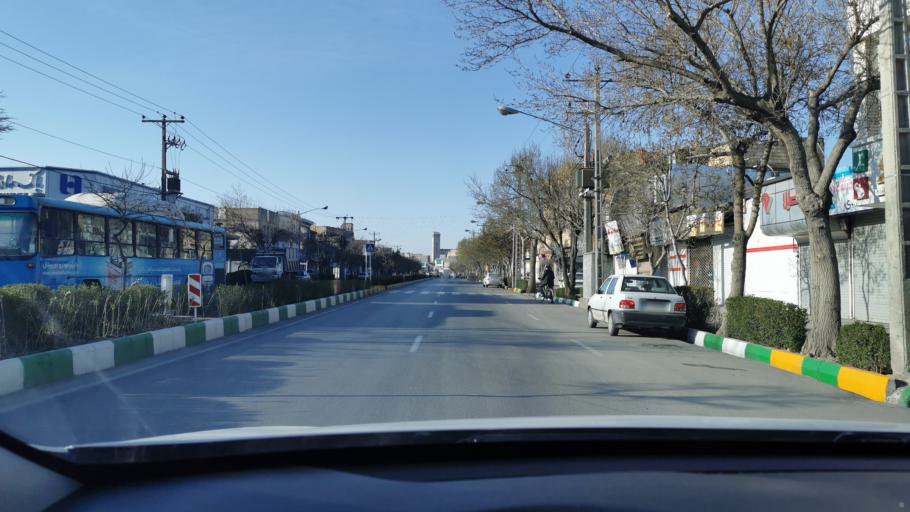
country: IR
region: Razavi Khorasan
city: Mashhad
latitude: 36.3099
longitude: 59.6362
